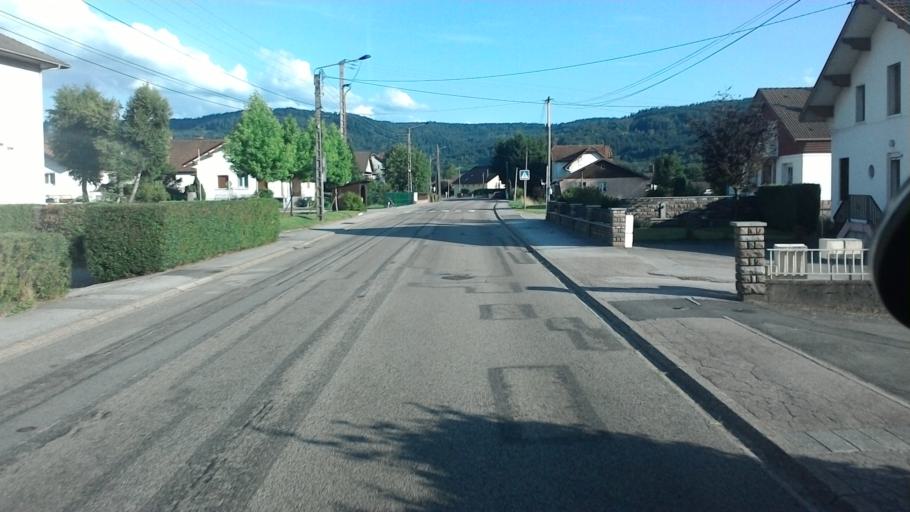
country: FR
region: Lorraine
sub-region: Departement des Vosges
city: Rupt-sur-Moselle
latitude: 47.9202
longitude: 6.6628
